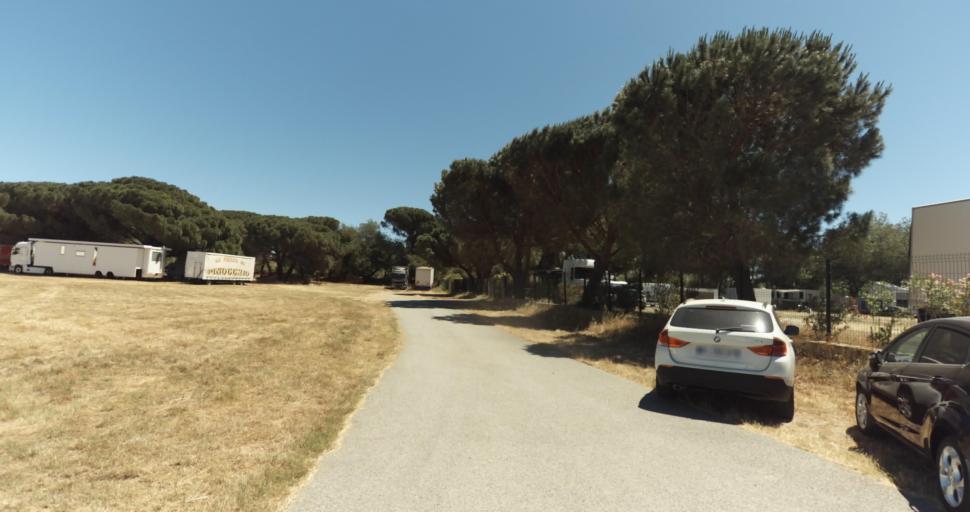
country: FR
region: Provence-Alpes-Cote d'Azur
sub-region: Departement du Var
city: Gassin
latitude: 43.2612
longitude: 6.5816
